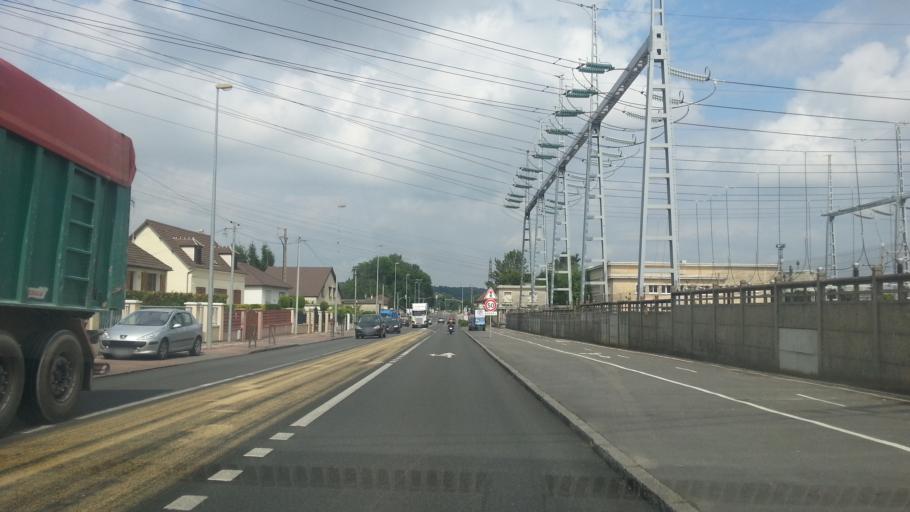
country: FR
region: Picardie
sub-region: Departement de l'Oise
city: Thiverny
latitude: 49.2422
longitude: 2.4400
